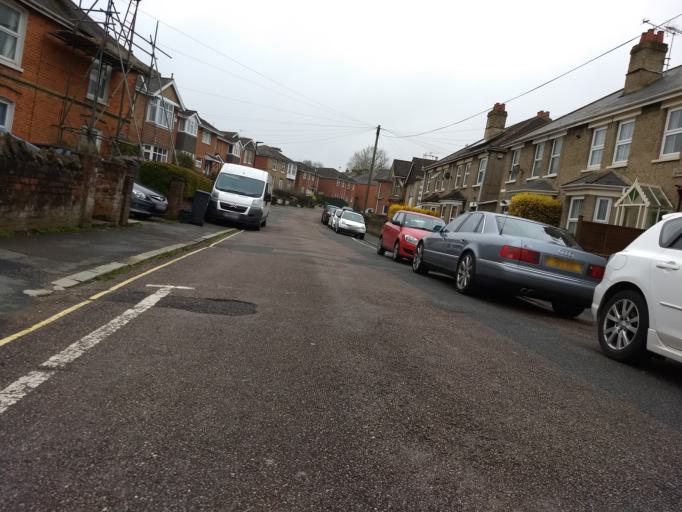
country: GB
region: England
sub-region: Isle of Wight
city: Ryde
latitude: 50.7256
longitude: -1.1526
